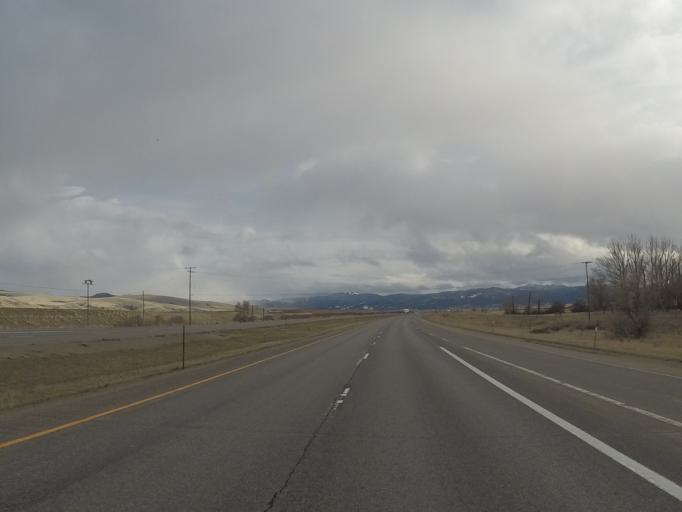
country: US
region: Montana
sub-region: Deer Lodge County
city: Warm Springs
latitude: 46.1788
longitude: -112.7845
